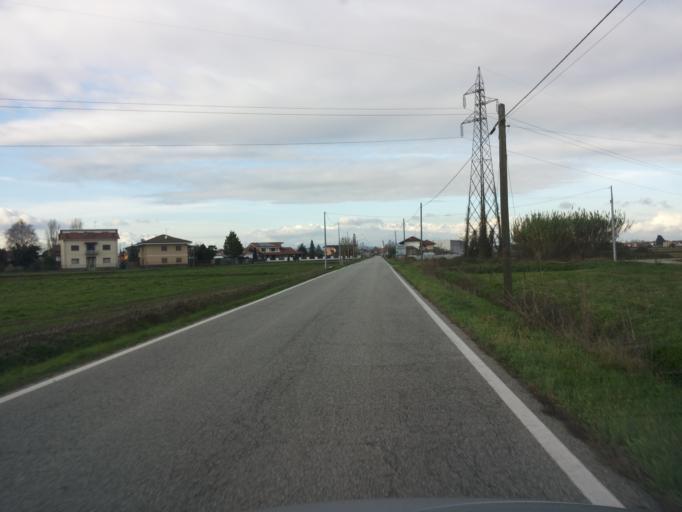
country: IT
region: Piedmont
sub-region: Provincia di Vercelli
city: Tronzano Vercellese
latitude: 45.3338
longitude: 8.1842
